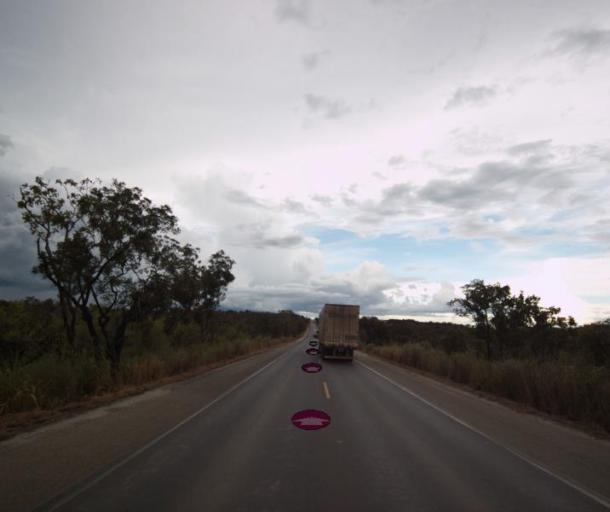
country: BR
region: Goias
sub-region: Itapaci
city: Itapaci
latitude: -14.9408
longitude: -49.3716
